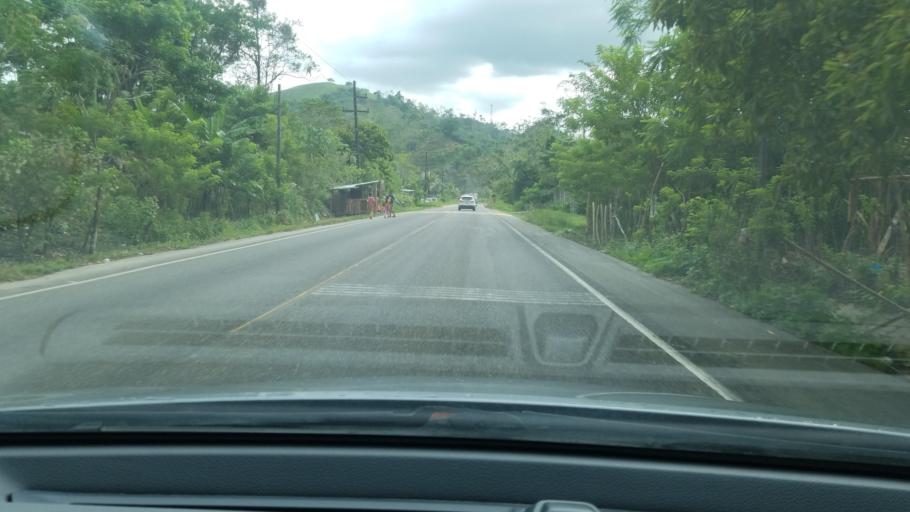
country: HN
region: Cortes
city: Potrerillos
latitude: 15.5945
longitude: -88.3064
